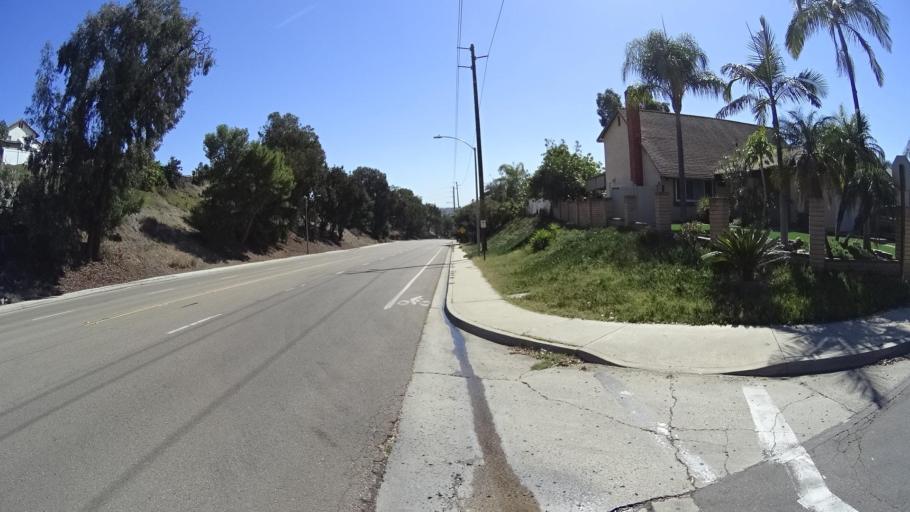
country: US
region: California
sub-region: San Diego County
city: La Presa
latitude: 32.6958
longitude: -117.0181
